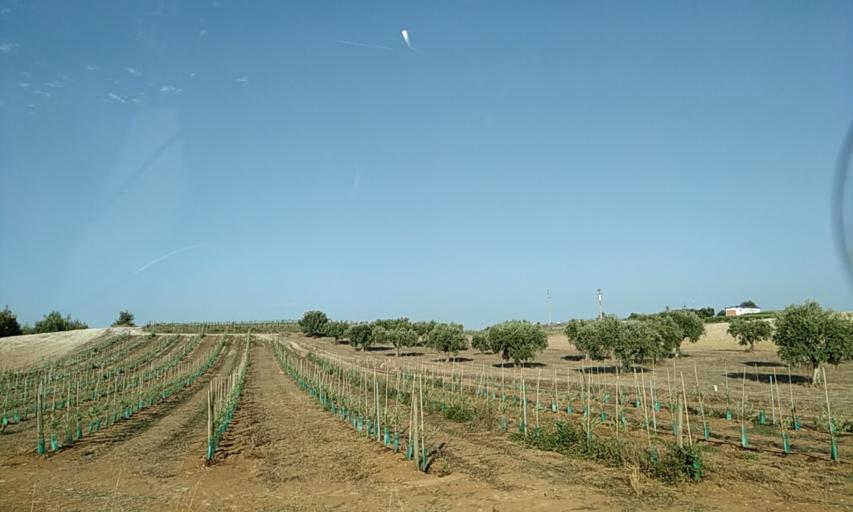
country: PT
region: Santarem
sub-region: Santarem
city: Santarem
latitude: 39.3289
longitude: -8.6622
